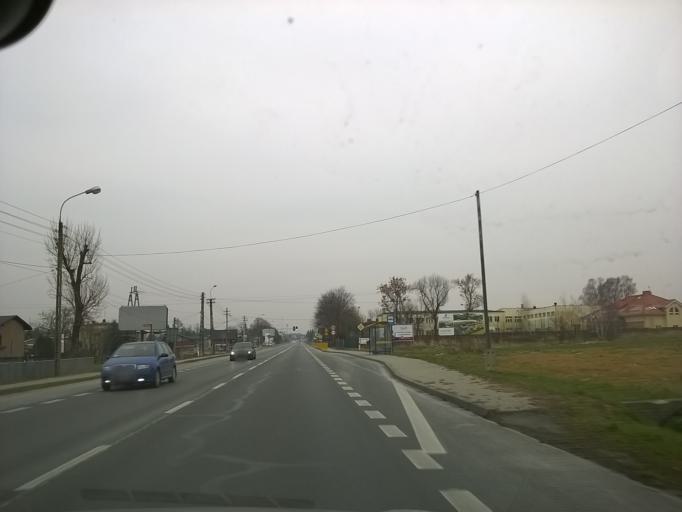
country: PL
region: Silesian Voivodeship
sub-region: Powiat gliwicki
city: Paniowki
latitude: 50.2245
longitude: 18.8156
